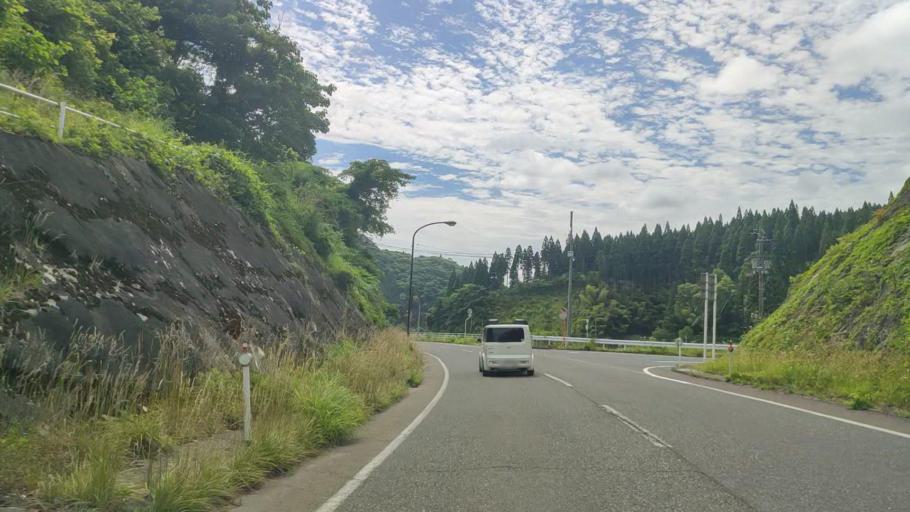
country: JP
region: Okayama
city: Niimi
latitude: 35.1731
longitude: 133.5724
